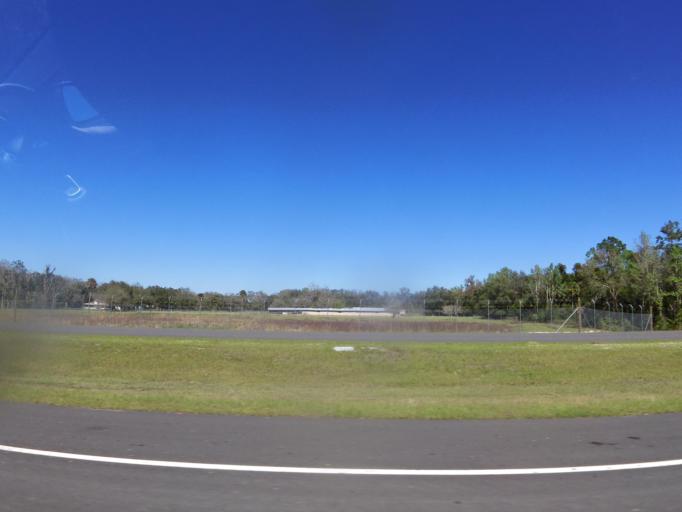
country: US
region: Florida
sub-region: Lake County
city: Mount Plymouth
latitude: 28.8149
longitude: -81.4814
